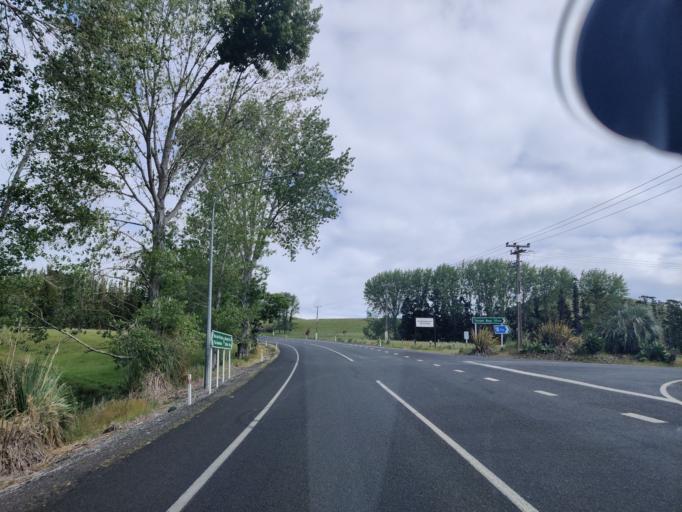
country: NZ
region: Northland
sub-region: Far North District
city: Taipa
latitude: -35.0013
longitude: 173.6184
